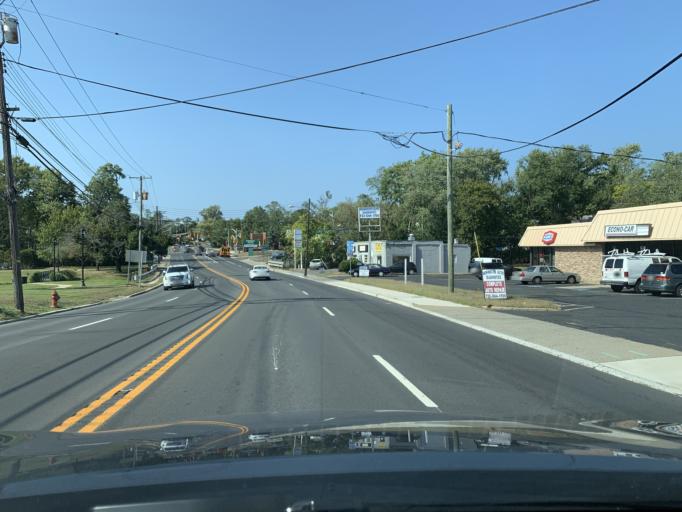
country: US
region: New Jersey
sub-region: Monmouth County
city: Eatontown
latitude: 40.3060
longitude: -74.0608
